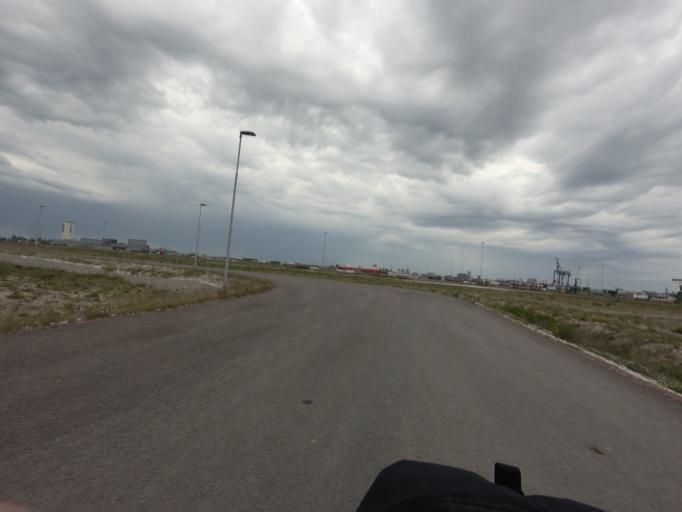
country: SE
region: Skane
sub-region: Malmo
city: Malmoe
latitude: 55.6317
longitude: 12.9950
